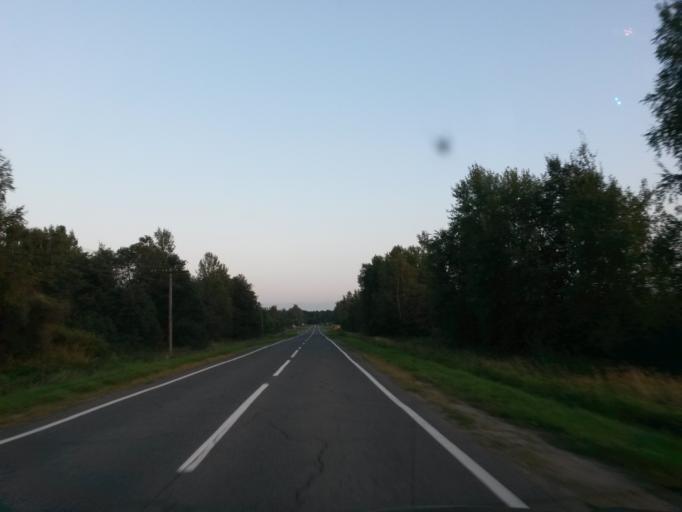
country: RU
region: Jaroslavl
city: Tutayev
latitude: 57.9319
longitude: 39.5029
